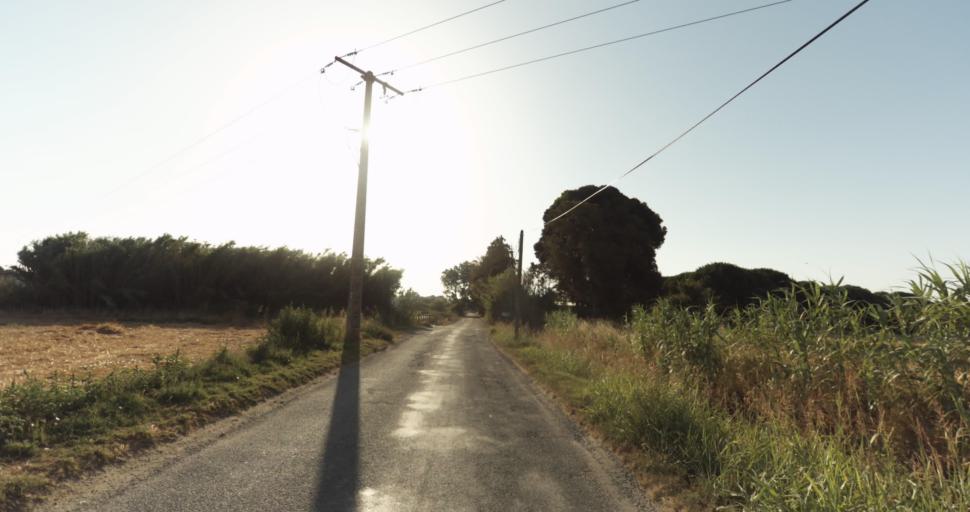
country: FR
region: Languedoc-Roussillon
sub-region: Departement des Pyrenees-Orientales
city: Latour-Bas-Elne
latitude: 42.5963
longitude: 3.0347
